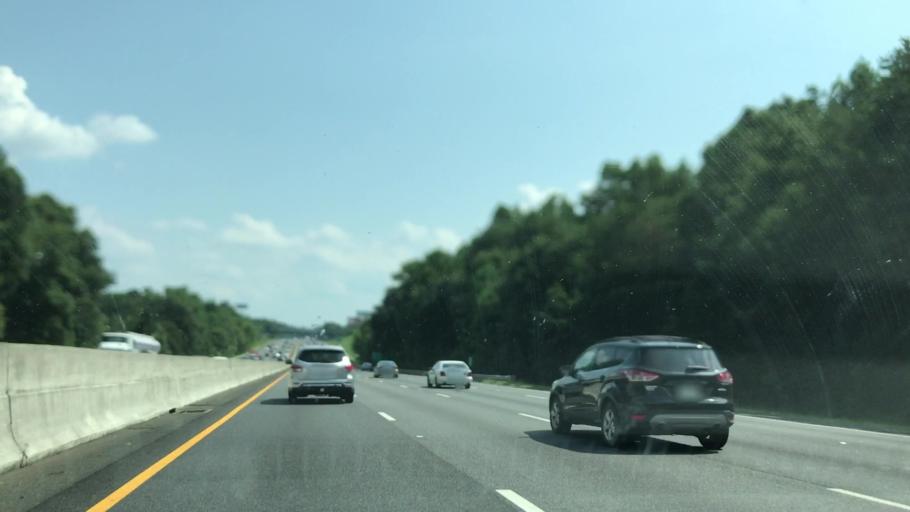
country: US
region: South Carolina
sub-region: York County
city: Fort Mill
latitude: 35.0501
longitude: -80.9588
